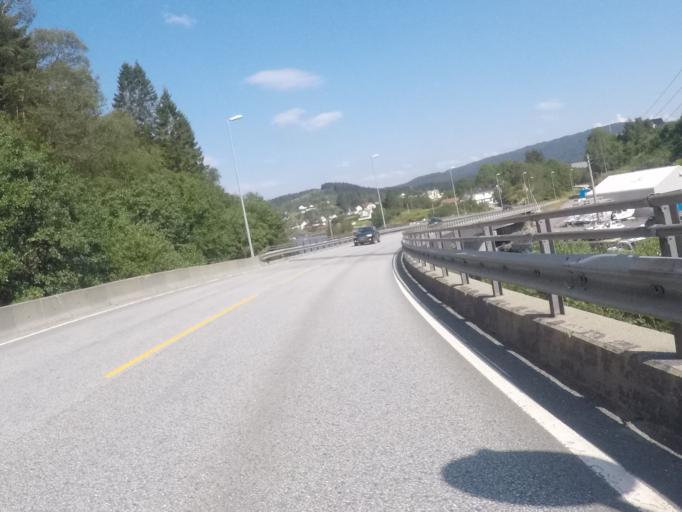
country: NO
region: Hordaland
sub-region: Bergen
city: Hylkje
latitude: 60.6028
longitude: 5.3970
